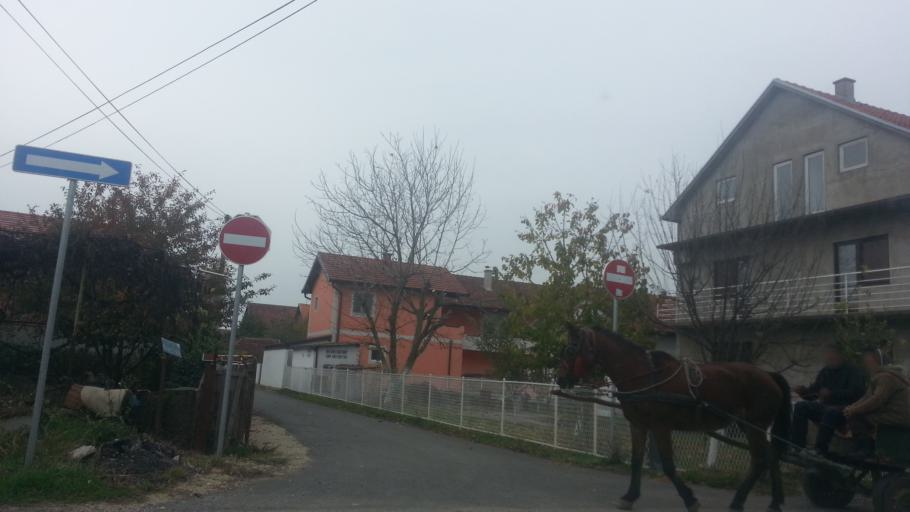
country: RS
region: Autonomna Pokrajina Vojvodina
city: Nova Pazova
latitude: 44.9555
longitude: 20.2158
